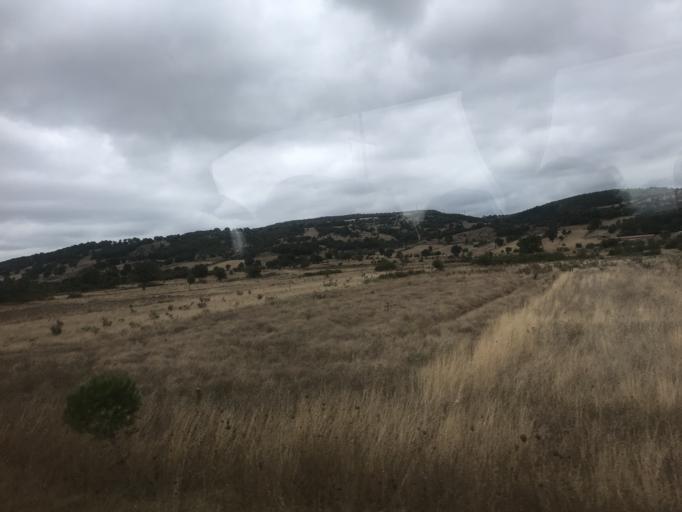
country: TR
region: Balikesir
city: Ergama
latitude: 39.6369
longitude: 27.6706
